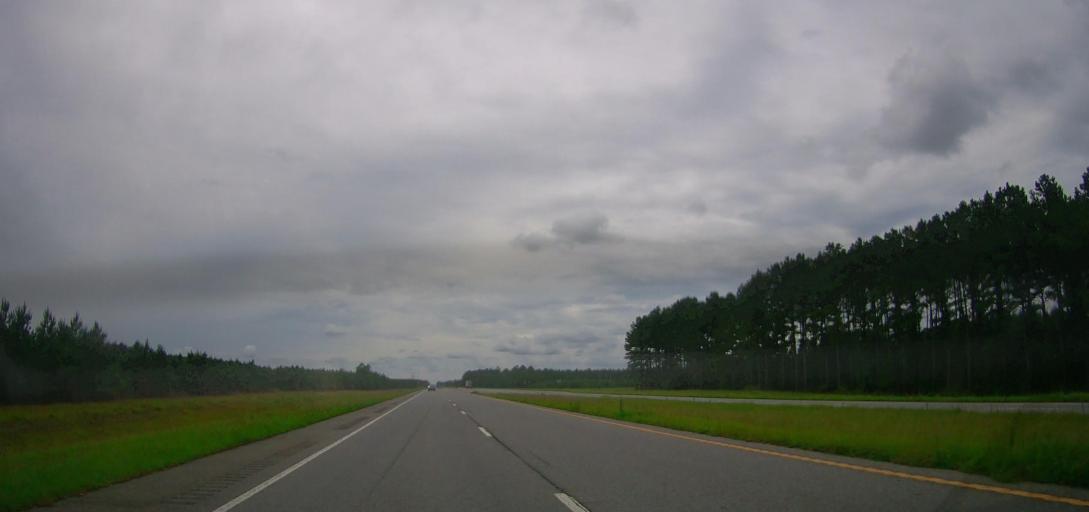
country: US
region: Georgia
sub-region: Appling County
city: Baxley
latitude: 31.7492
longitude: -82.2643
